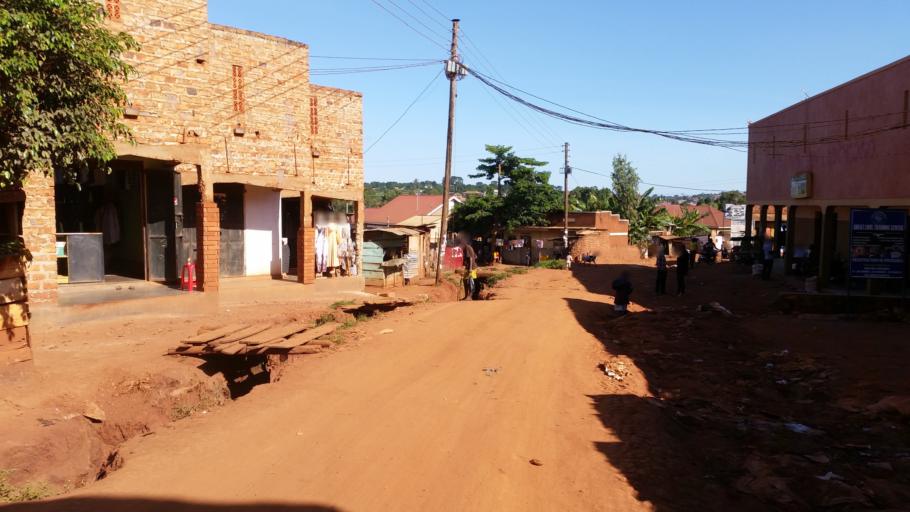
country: UG
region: Central Region
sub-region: Wakiso District
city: Kireka
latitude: 0.3317
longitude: 32.6527
